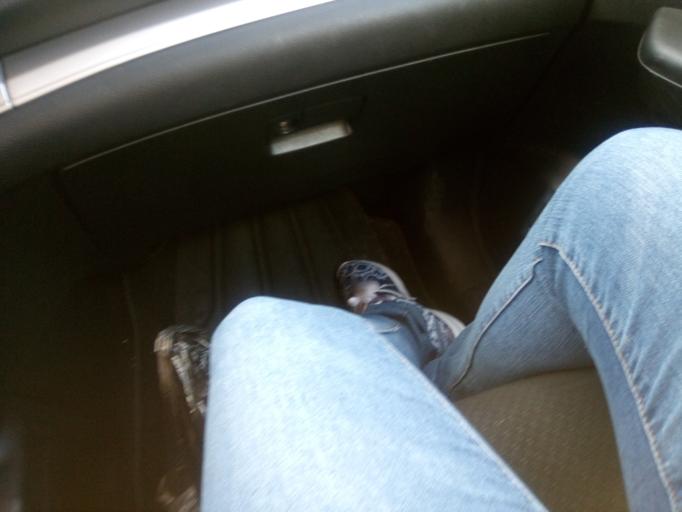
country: MX
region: Jalisco
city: Guadalajara
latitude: 20.6725
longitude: -103.4062
